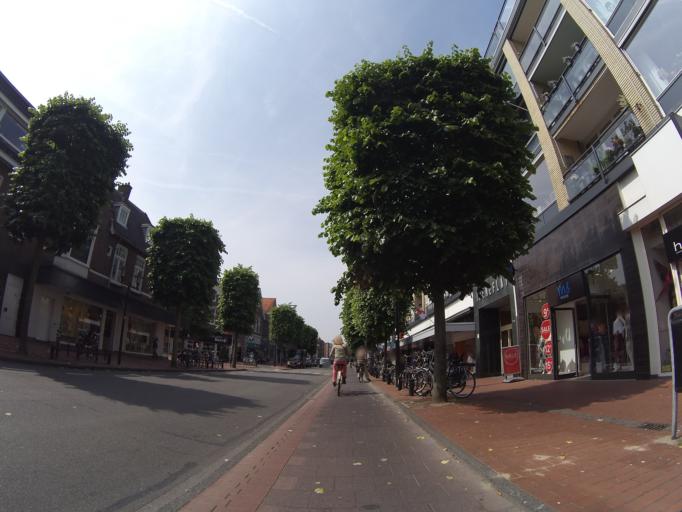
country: NL
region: Utrecht
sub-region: Gemeente Zeist
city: Zeist
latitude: 52.0855
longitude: 5.2440
